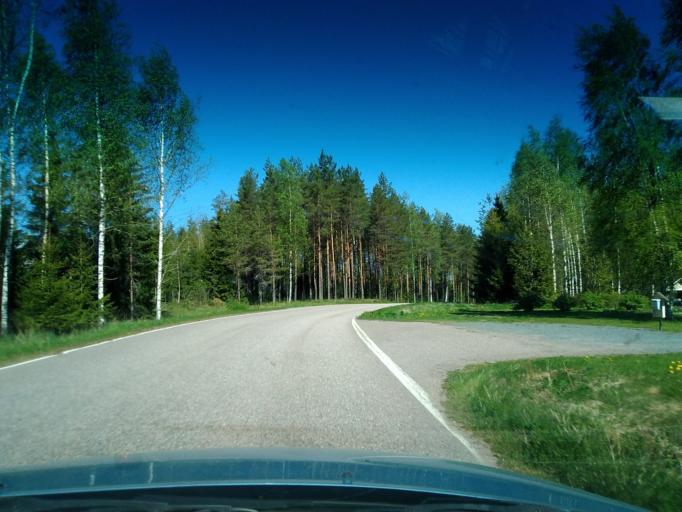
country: FI
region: Uusimaa
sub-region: Helsinki
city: Kaerkoelae
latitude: 60.6412
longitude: 23.9262
